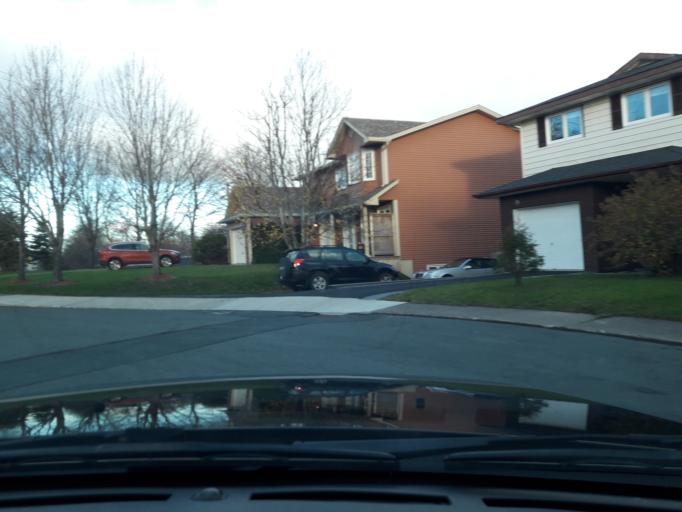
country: CA
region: Newfoundland and Labrador
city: St. John's
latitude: 47.5648
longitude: -52.7525
